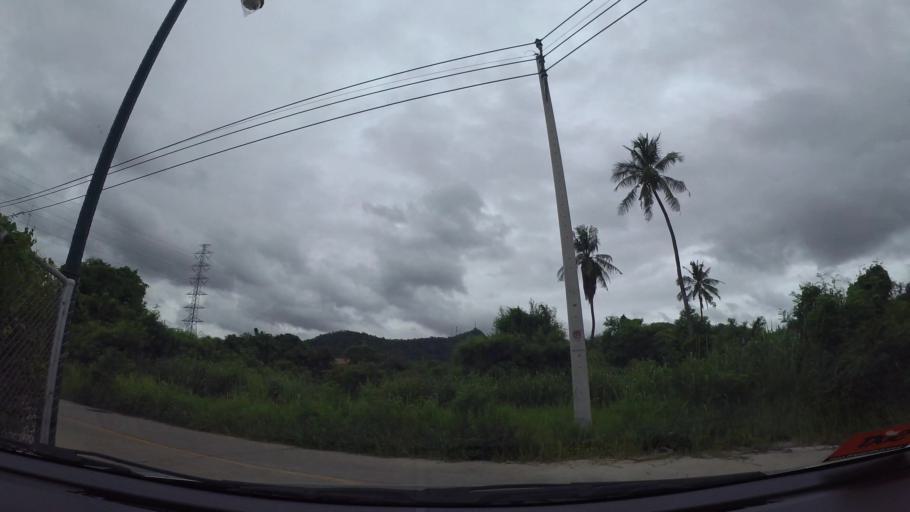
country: TH
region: Chon Buri
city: Si Racha
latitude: 13.2063
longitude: 100.9492
